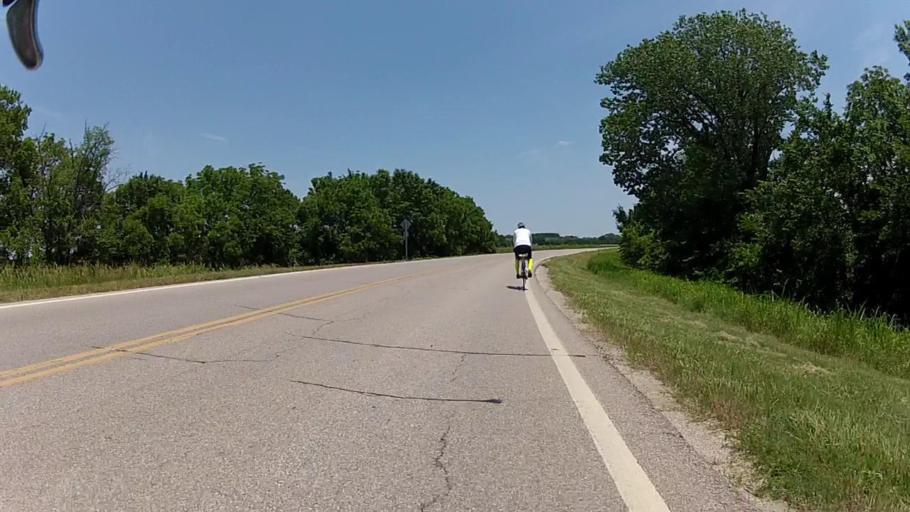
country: US
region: Kansas
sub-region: Chautauqua County
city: Sedan
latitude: 37.1197
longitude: -96.2145
